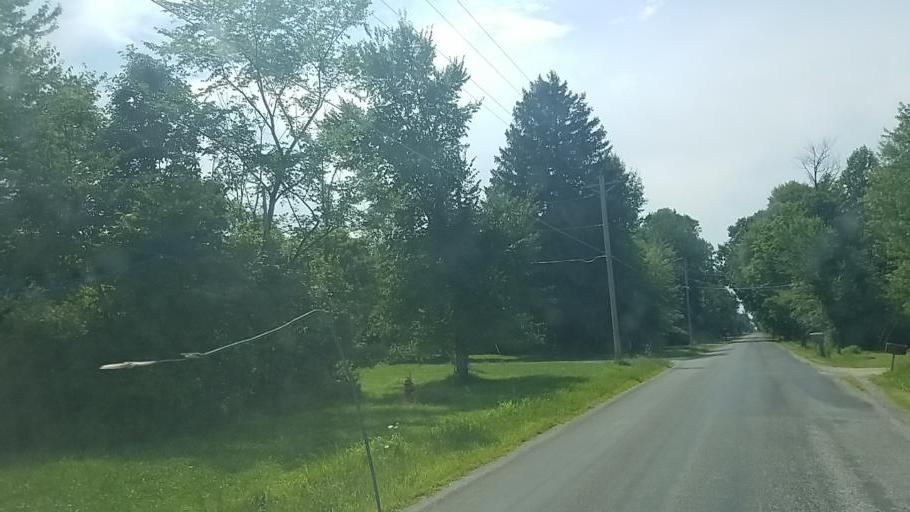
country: US
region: Ohio
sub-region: Medina County
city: Lodi
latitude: 41.0905
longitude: -81.9795
